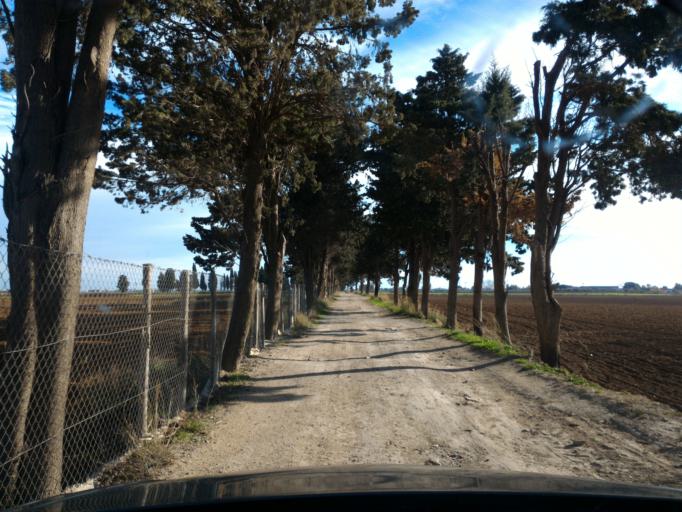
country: IT
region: Calabria
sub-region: Provincia di Crotone
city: Isola di Capo Rizzuto
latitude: 38.9871
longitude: 17.0671
